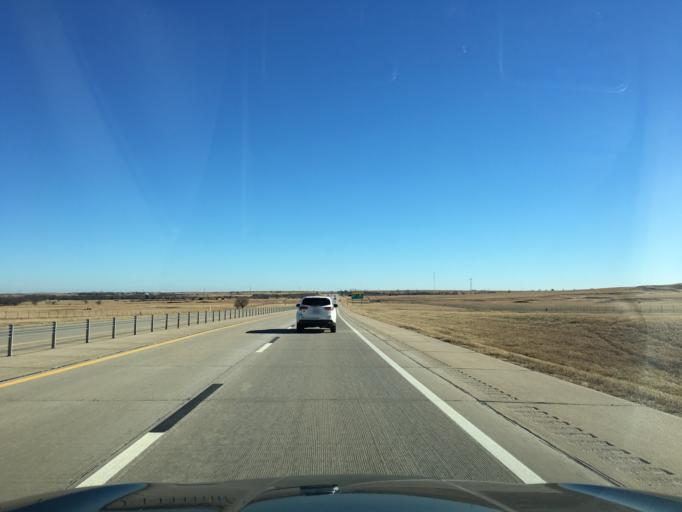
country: US
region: Oklahoma
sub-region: Noble County
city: Perry
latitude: 36.3904
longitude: -97.0986
